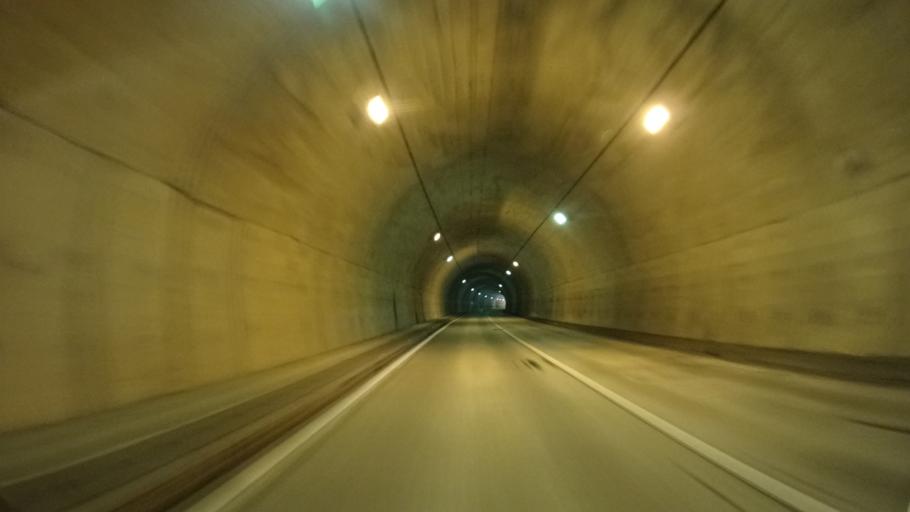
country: JP
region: Ehime
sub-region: Nishiuwa-gun
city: Ikata-cho
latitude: 33.4374
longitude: 132.2355
